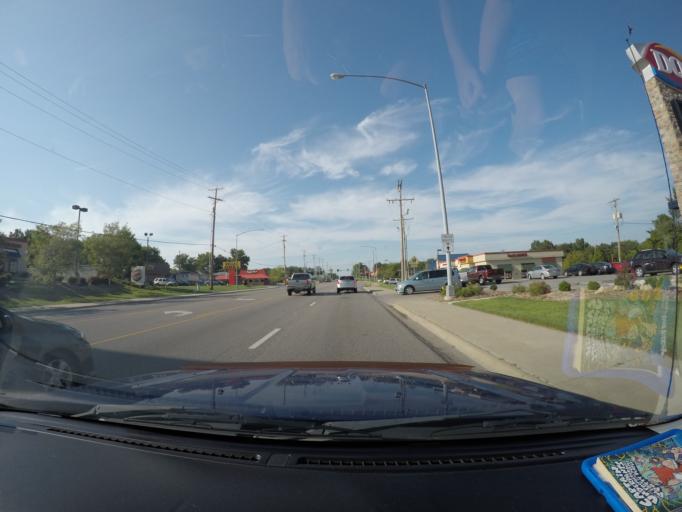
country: US
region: Kansas
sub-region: Leavenworth County
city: Lansing
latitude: 39.2559
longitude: -94.8999
